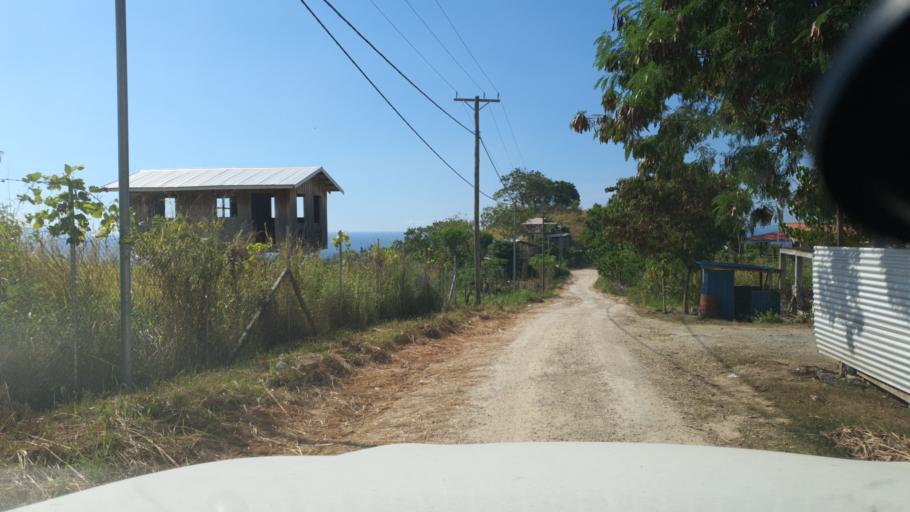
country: SB
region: Guadalcanal
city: Honiara
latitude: -9.4605
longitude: 159.9758
